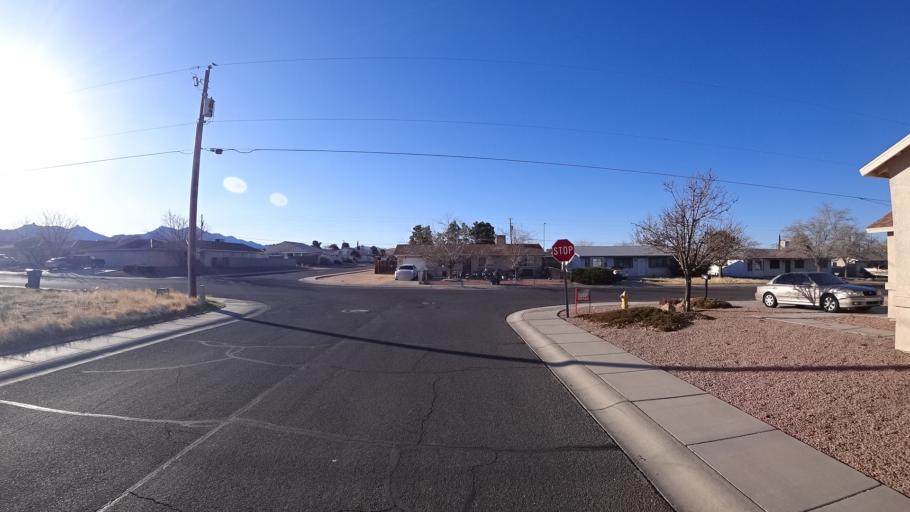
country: US
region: Arizona
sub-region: Mohave County
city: Kingman
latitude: 35.1961
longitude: -114.0159
